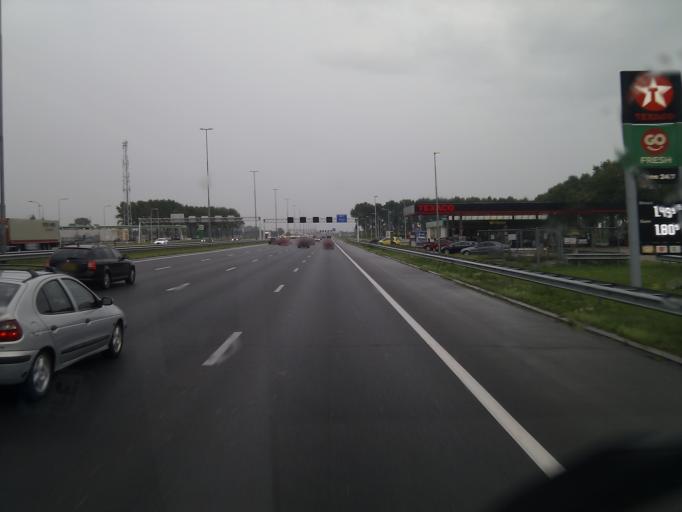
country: NL
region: Gelderland
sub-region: Gemeente Culemborg
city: Culemborg
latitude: 51.9134
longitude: 5.1784
